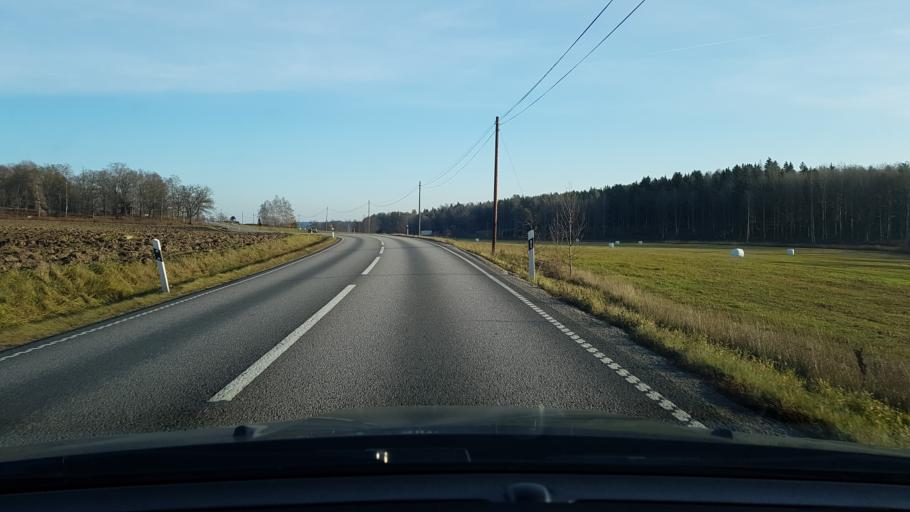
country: SE
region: Stockholm
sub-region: Norrtalje Kommun
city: Nykvarn
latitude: 59.7349
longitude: 18.2755
